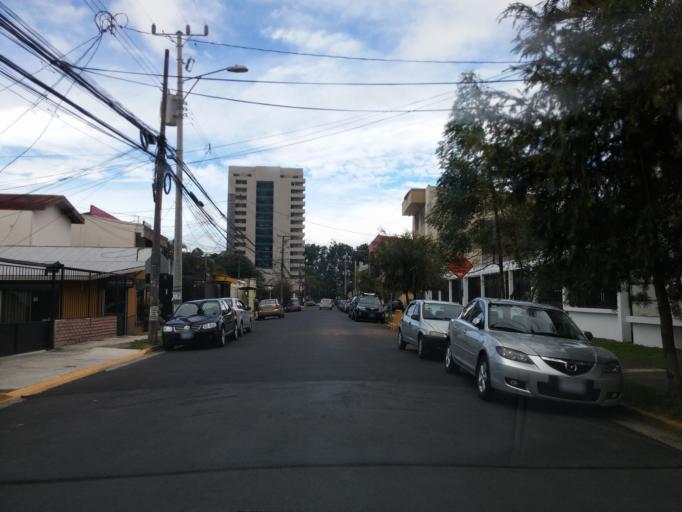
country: CR
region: San Jose
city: San Jose
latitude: 9.9308
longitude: -84.1089
